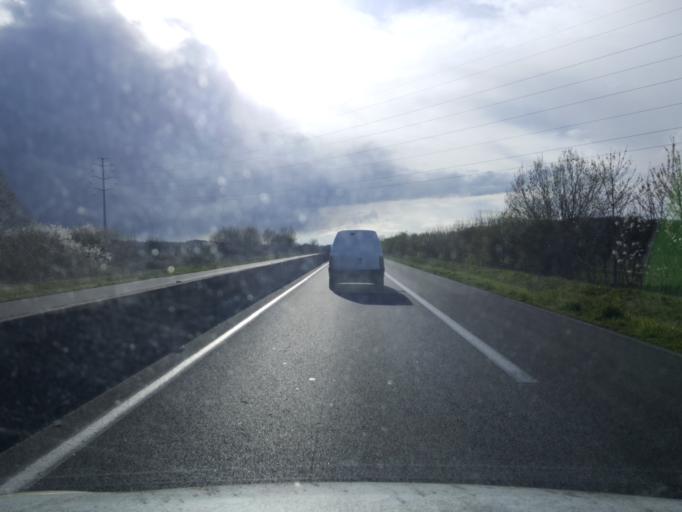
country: FR
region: Picardie
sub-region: Departement de l'Oise
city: Auneuil
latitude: 49.3829
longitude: 2.0354
